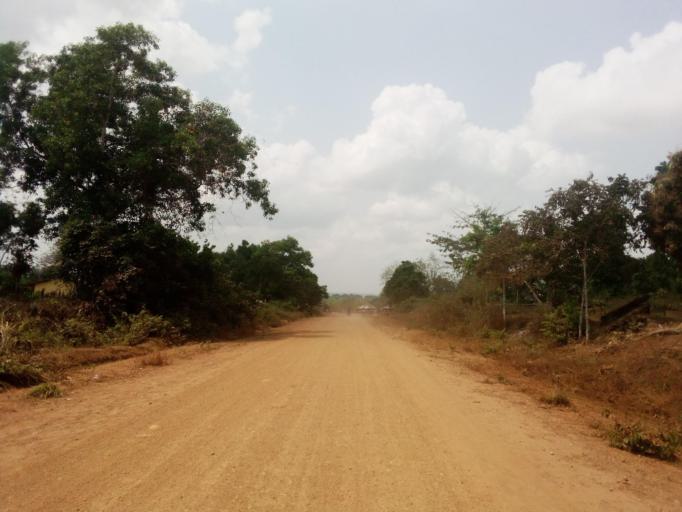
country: SL
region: Southern Province
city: Mogbwemo
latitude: 7.6647
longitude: -12.2754
